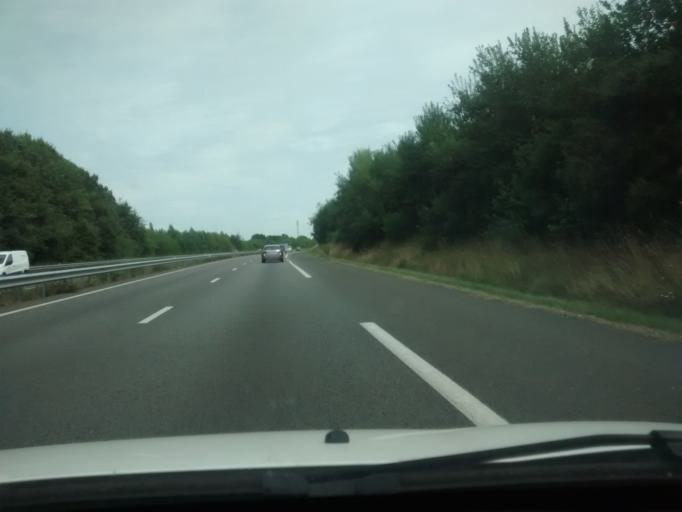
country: FR
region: Brittany
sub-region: Departement d'Ille-et-Vilaine
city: Liffre
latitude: 48.2100
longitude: -1.5221
